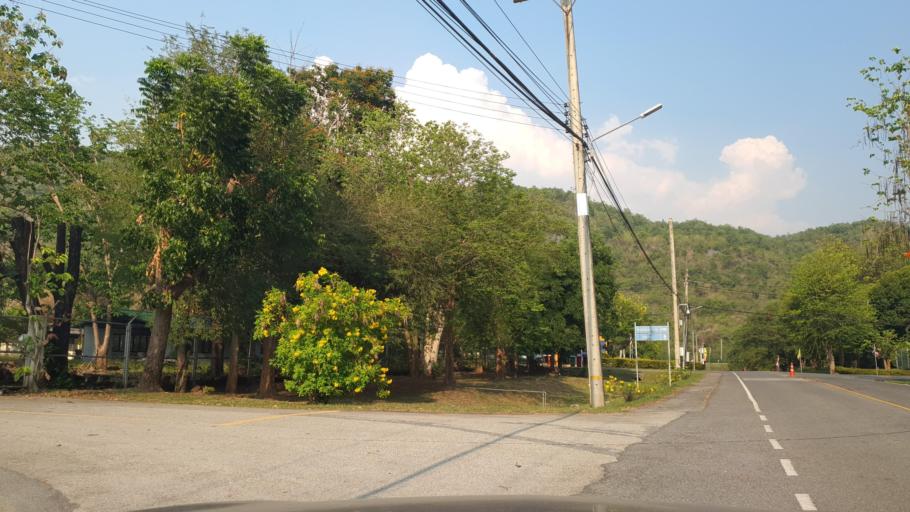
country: TH
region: Kanchanaburi
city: Sai Yok
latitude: 14.2298
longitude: 99.2359
